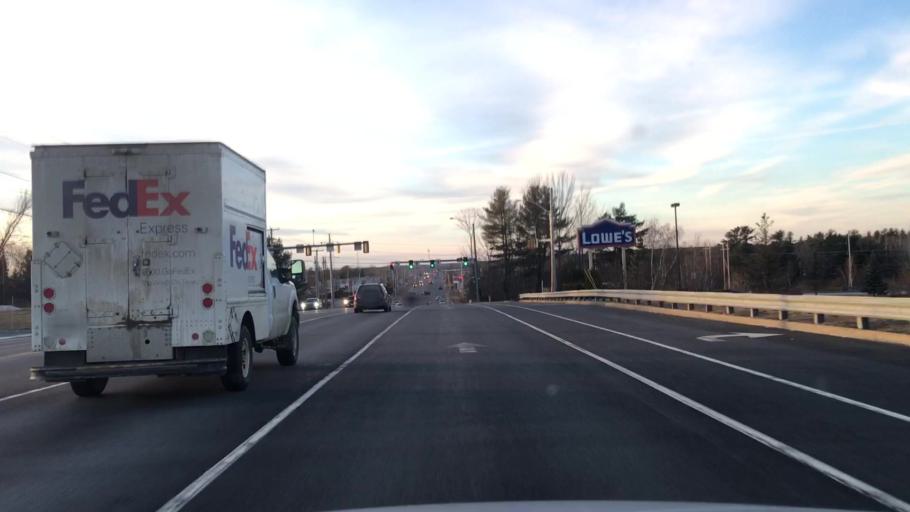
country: US
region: Maine
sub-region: Penobscot County
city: Brewer
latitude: 44.7735
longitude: -68.7265
